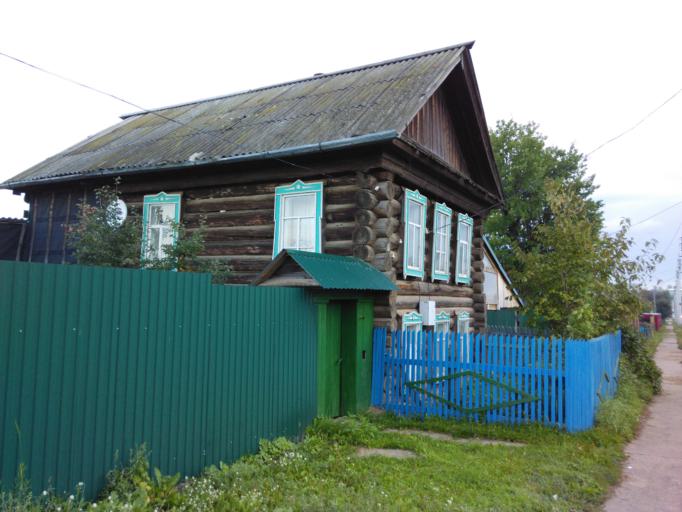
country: RU
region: Perm
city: Foki
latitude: 56.6963
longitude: 54.3522
